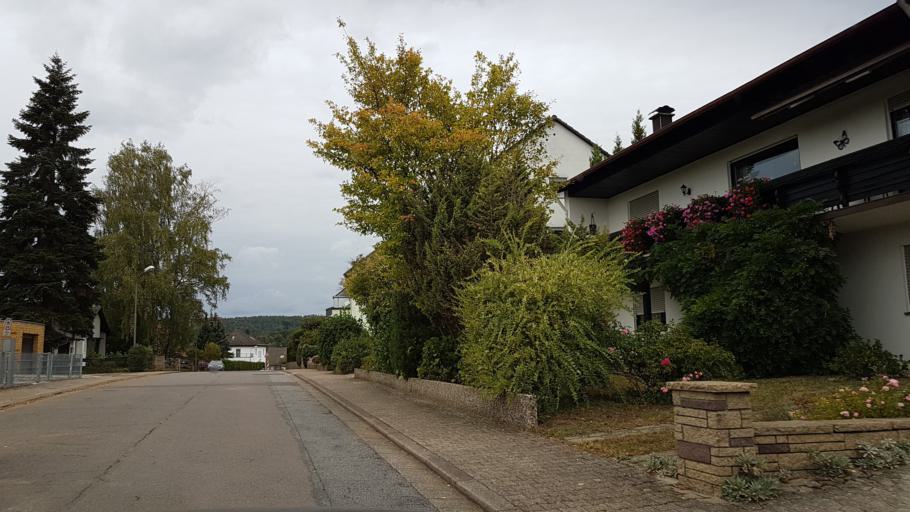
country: DE
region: Saarland
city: Homburg
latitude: 49.2725
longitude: 7.3178
